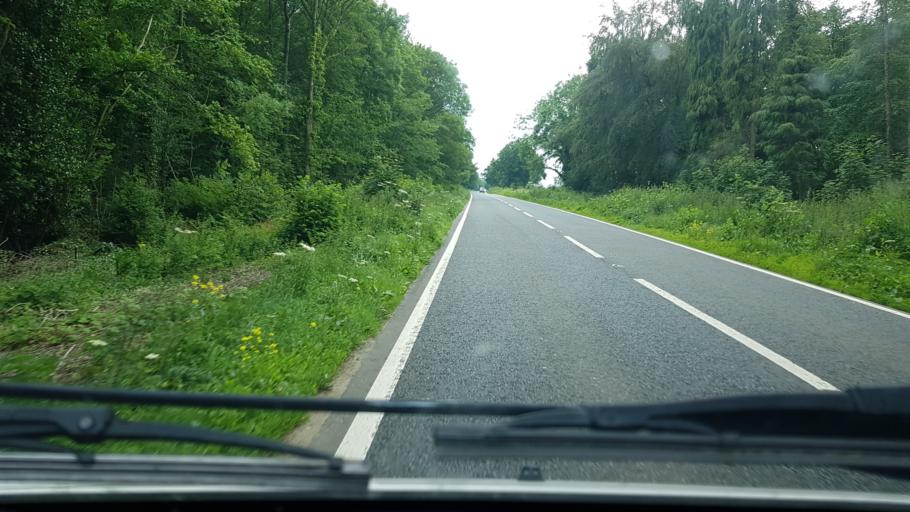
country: GB
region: England
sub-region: Gloucestershire
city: Chipping Campden
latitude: 52.0036
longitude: -1.7874
